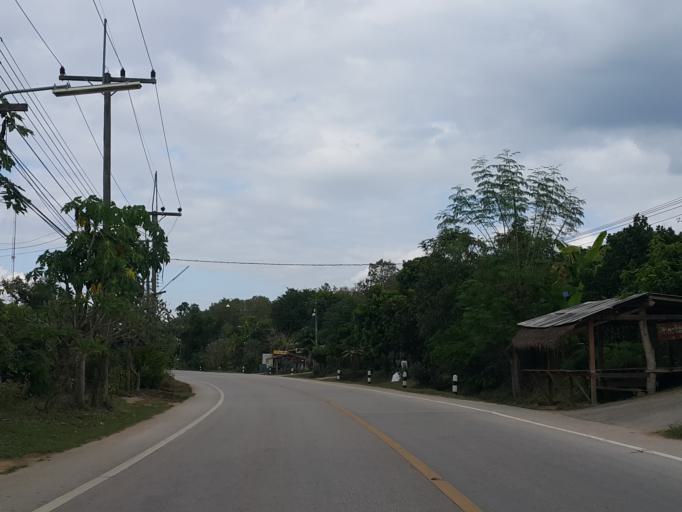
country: TH
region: Lampang
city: Chae Hom
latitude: 18.5849
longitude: 99.4722
